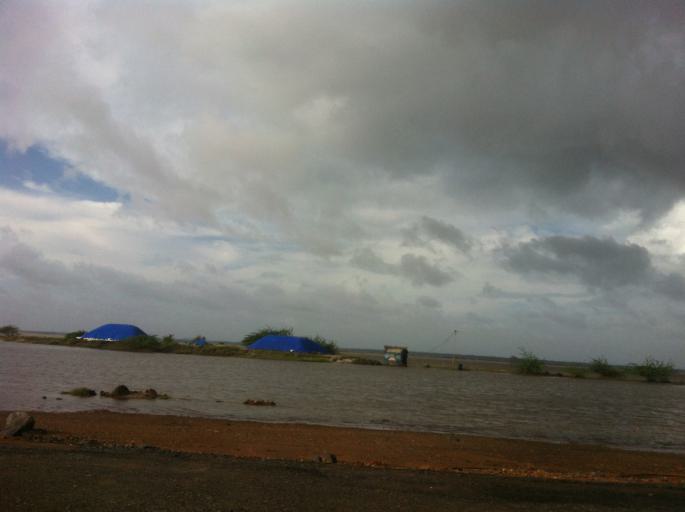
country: IN
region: Tamil Nadu
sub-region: Villupuram
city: Marakkanam
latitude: 12.1997
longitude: 79.9616
